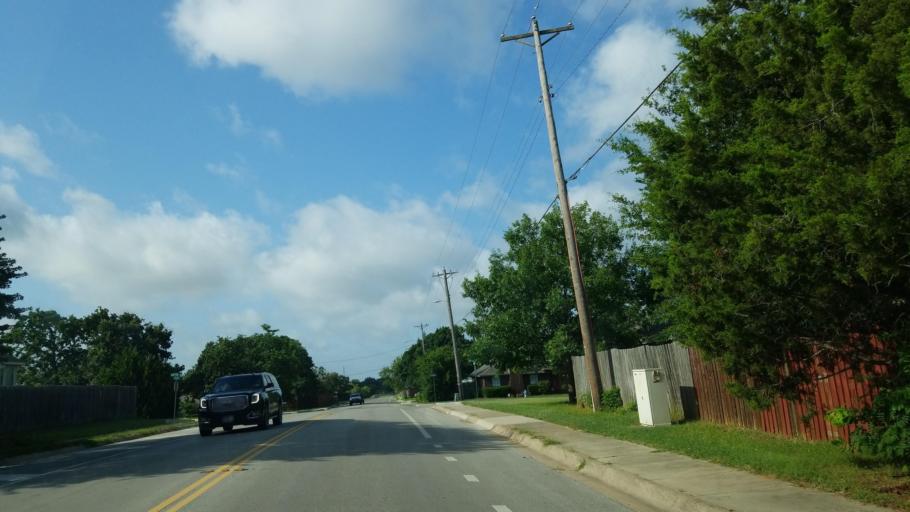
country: US
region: Texas
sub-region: Denton County
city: Denton
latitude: 33.2267
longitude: -97.0977
